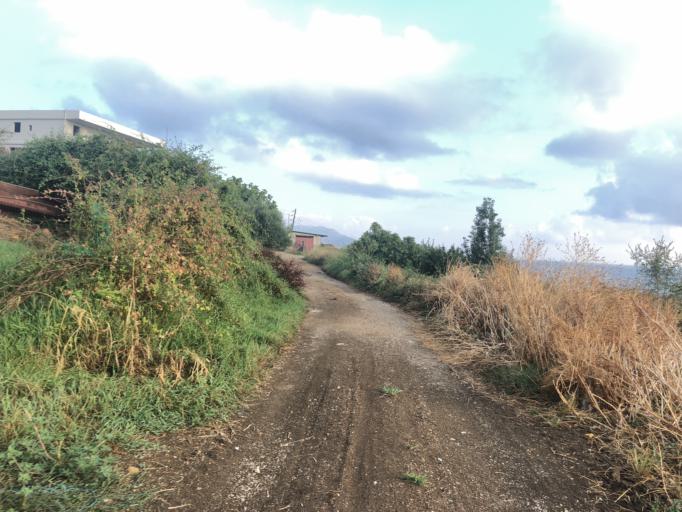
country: GR
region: Crete
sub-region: Nomos Chanias
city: Georgioupolis
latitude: 35.3463
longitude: 24.3121
